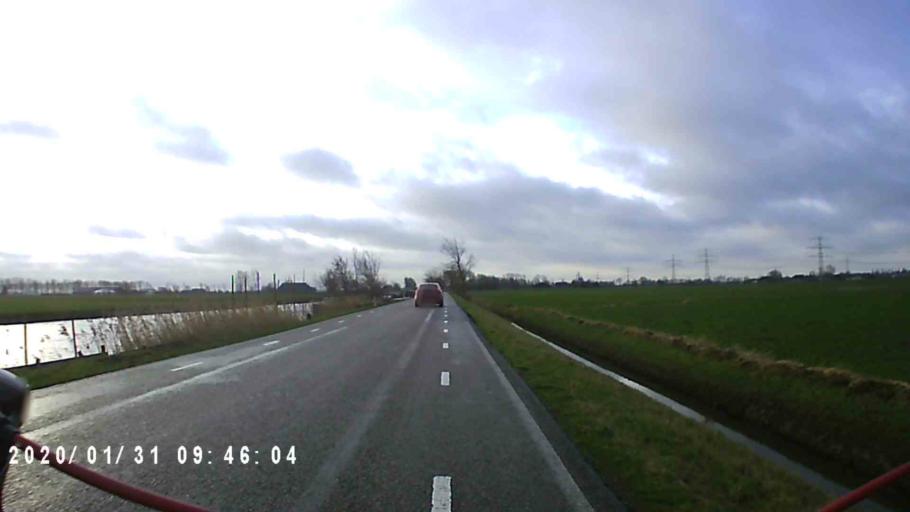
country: NL
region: Groningen
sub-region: Gemeente Zuidhorn
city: Aduard
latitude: 53.2673
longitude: 6.4833
